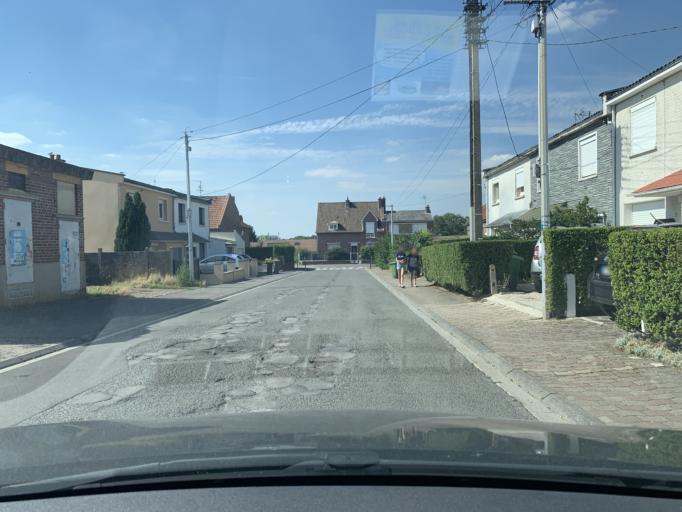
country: FR
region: Nord-Pas-de-Calais
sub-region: Departement du Nord
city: Cambrai
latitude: 50.1602
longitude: 3.2476
